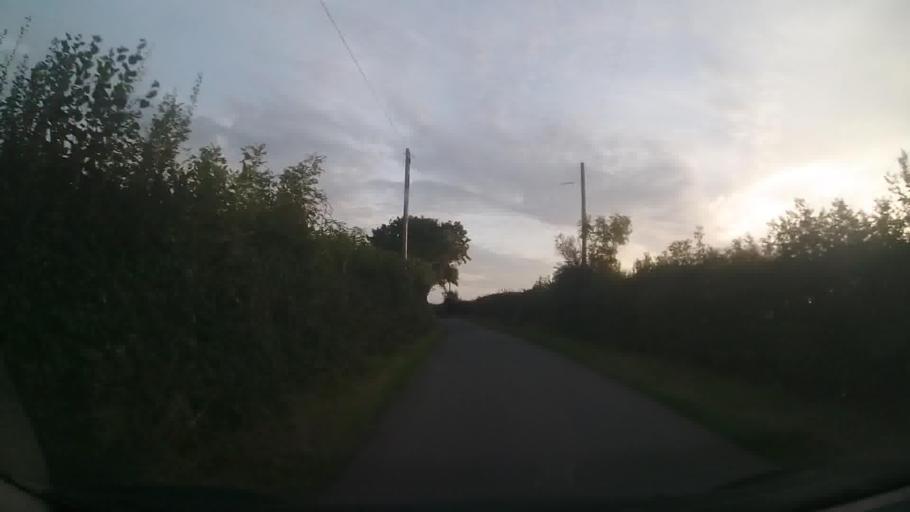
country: GB
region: Wales
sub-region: Pembrokeshire
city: Saundersfoot
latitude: 51.7492
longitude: -4.6555
